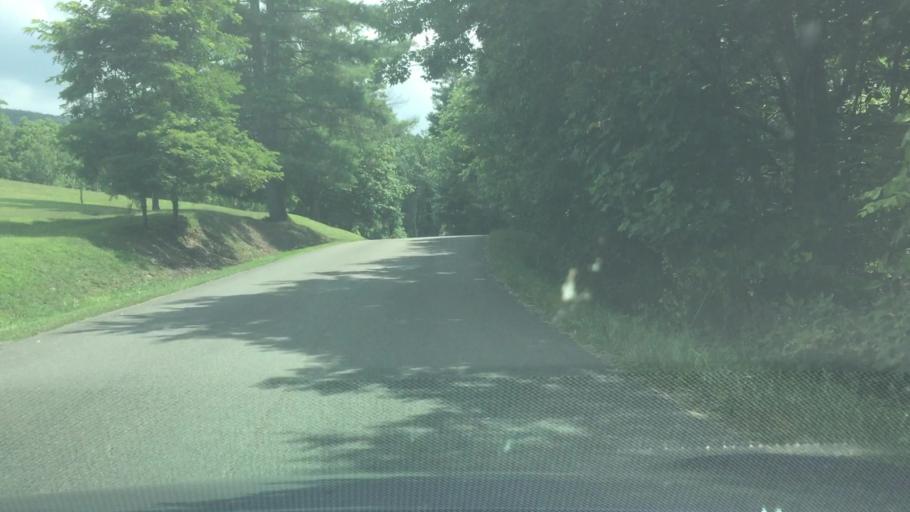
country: US
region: Virginia
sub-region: Wythe County
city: Wytheville
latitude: 36.9258
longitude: -81.0308
